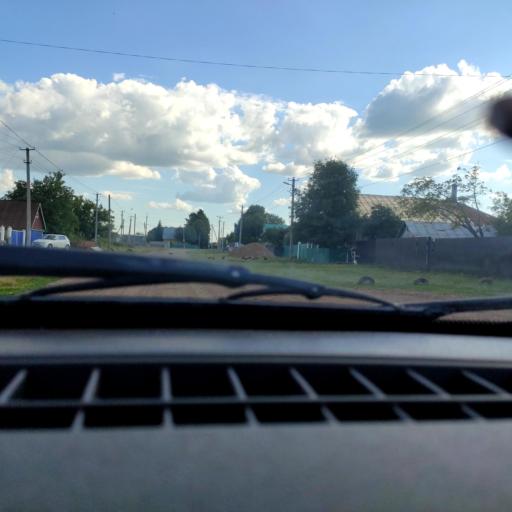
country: RU
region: Bashkortostan
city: Mikhaylovka
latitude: 54.9504
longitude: 55.7655
